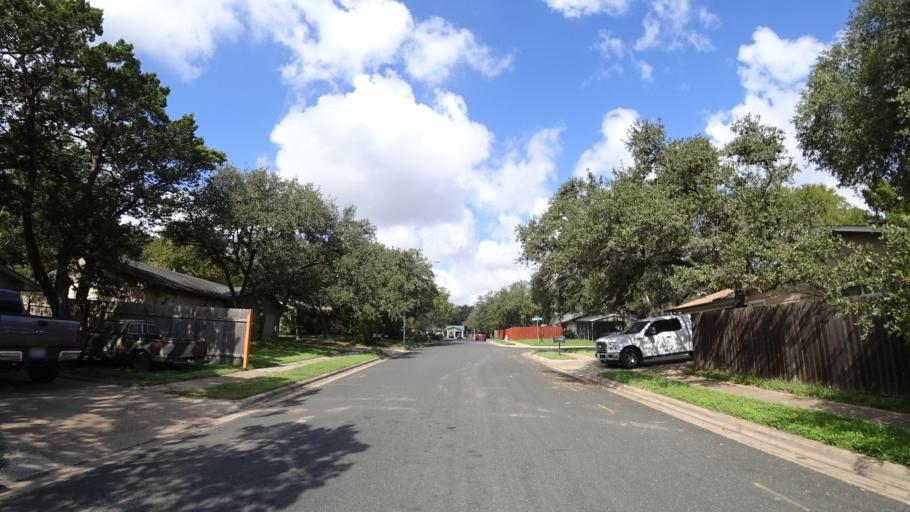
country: US
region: Texas
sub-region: Travis County
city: Shady Hollow
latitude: 30.2004
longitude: -97.8131
